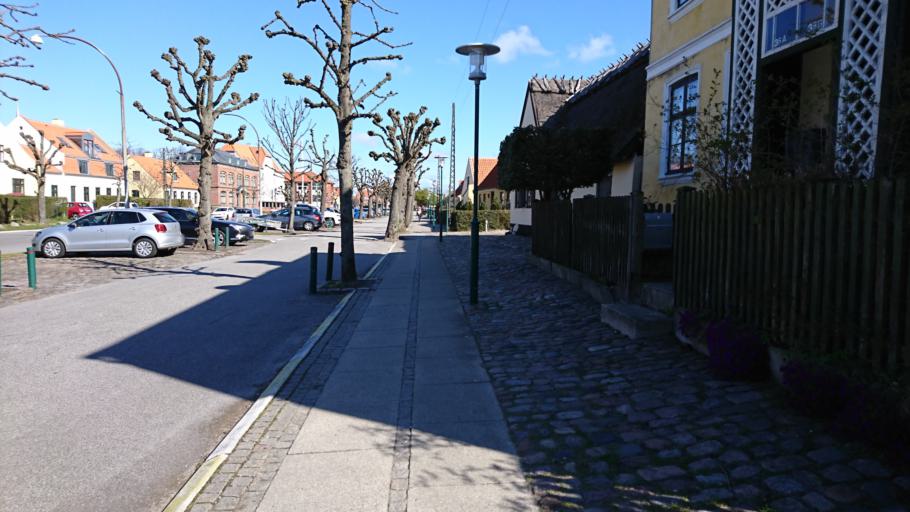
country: DK
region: Capital Region
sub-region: Dragor Kommune
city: Dragor
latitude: 55.5921
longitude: 12.6706
